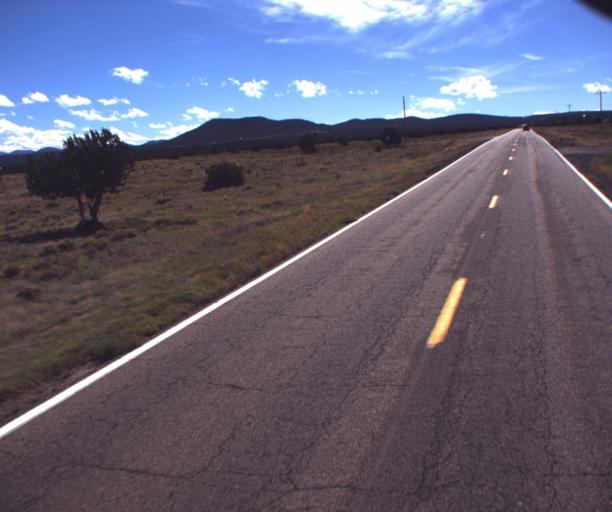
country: US
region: Arizona
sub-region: Navajo County
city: White Mountain Lake
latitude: 34.3453
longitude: -109.7272
